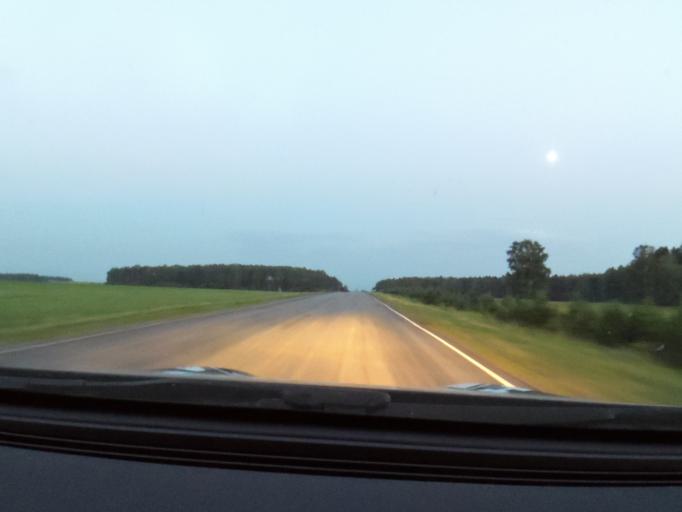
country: RU
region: Bashkortostan
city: Duvan
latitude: 56.0936
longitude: 58.0716
